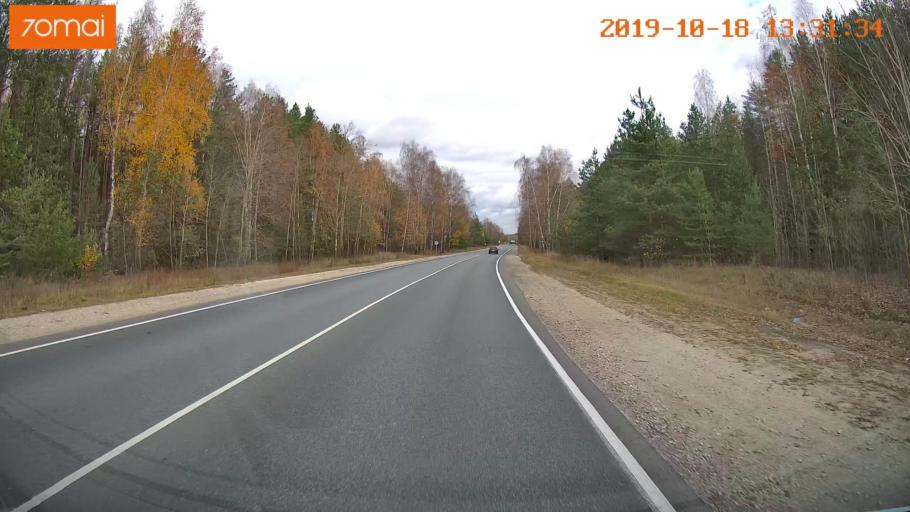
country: RU
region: Rjazan
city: Solotcha
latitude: 54.8237
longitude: 39.9024
